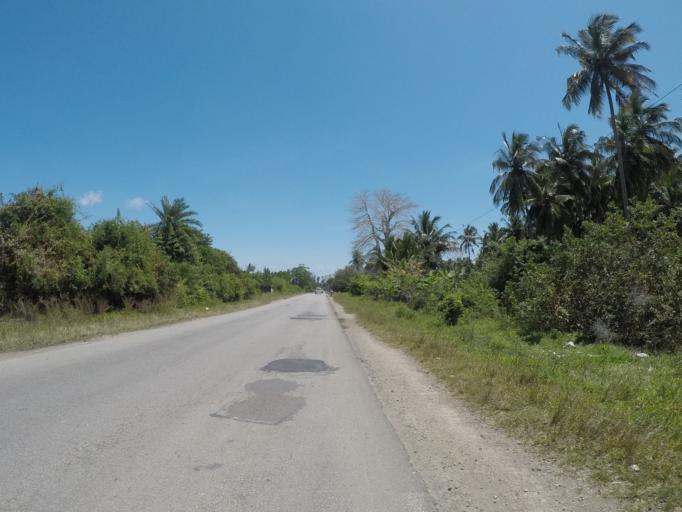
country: TZ
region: Zanzibar Central/South
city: Nganane
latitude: -6.2702
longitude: 39.4250
